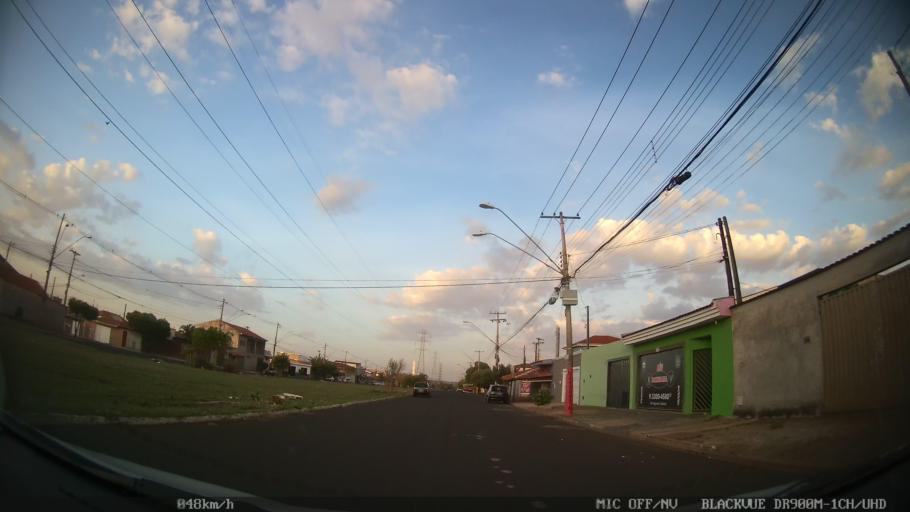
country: BR
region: Sao Paulo
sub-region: Ribeirao Preto
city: Ribeirao Preto
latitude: -21.1199
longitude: -47.8219
